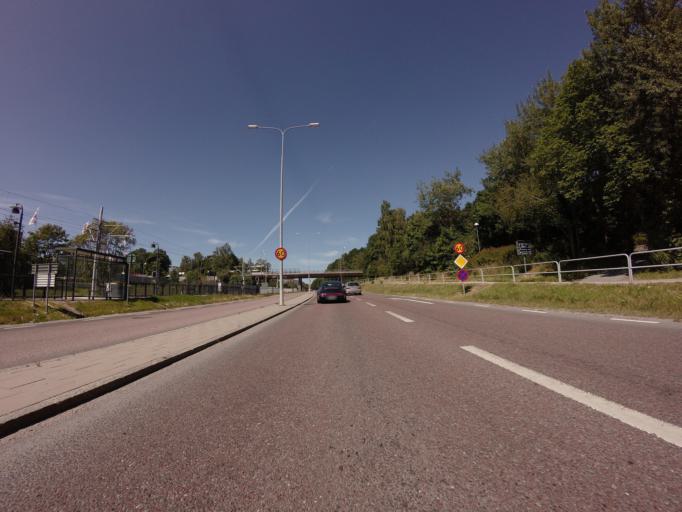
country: SE
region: Stockholm
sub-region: Lidingo
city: Lidingoe
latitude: 59.3505
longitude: 18.1468
